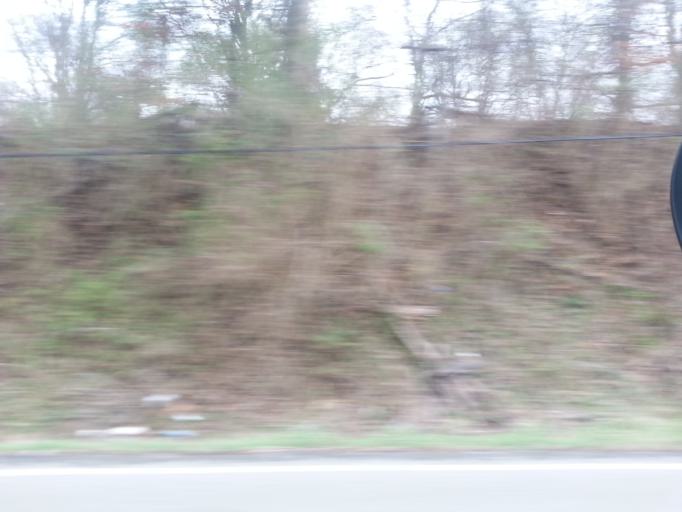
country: US
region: Tennessee
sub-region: Union County
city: Condon
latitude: 36.1194
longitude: -83.8651
